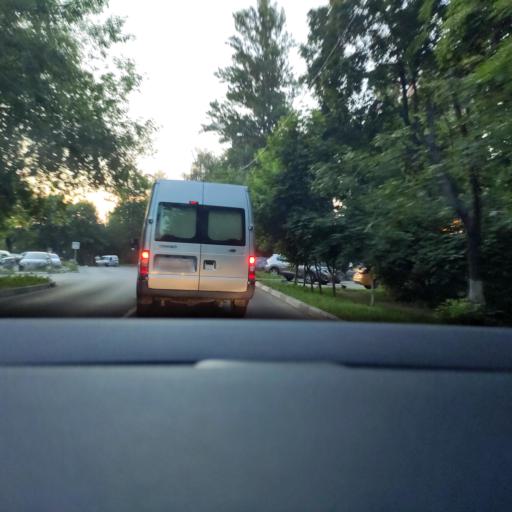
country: RU
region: Moskovskaya
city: Zheleznodorozhnyy
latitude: 55.7486
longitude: 37.9863
